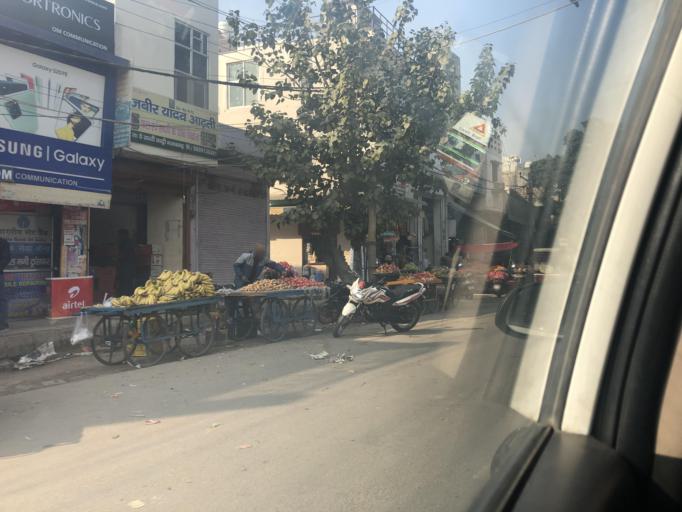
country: IN
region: Haryana
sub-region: Jhajjar
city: Bahadurgarh
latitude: 28.6145
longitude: 76.9781
